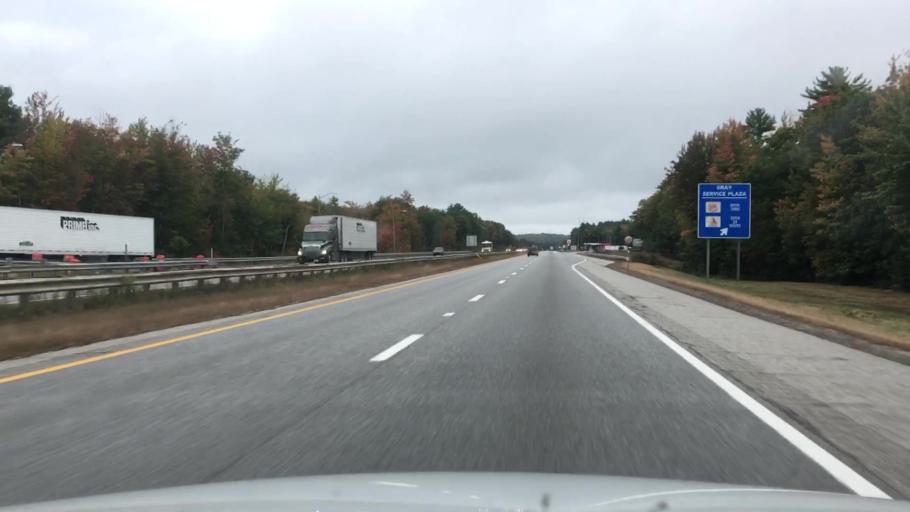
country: US
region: Maine
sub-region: Cumberland County
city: Cumberland Center
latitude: 43.8192
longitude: -70.3193
